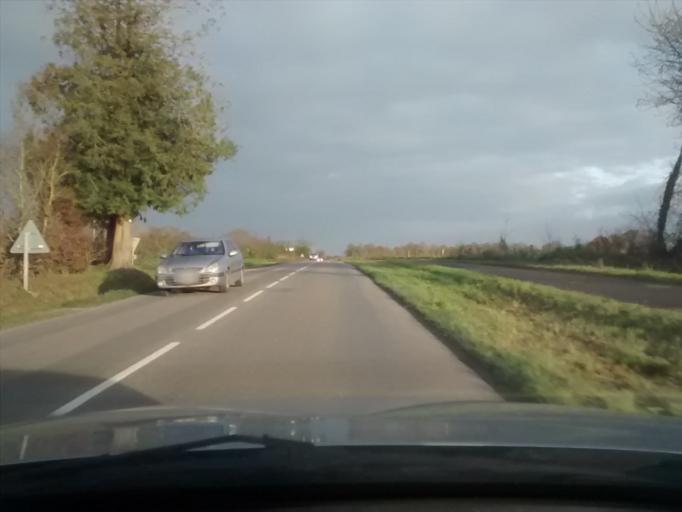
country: FR
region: Pays de la Loire
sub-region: Departement de la Mayenne
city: Change
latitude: 48.1023
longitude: -0.7665
